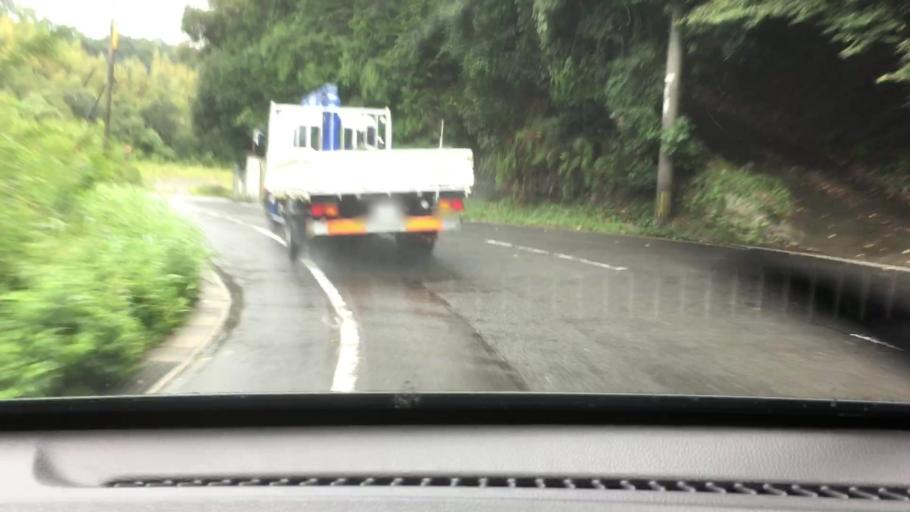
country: JP
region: Nagasaki
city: Togitsu
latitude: 32.8587
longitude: 129.7778
